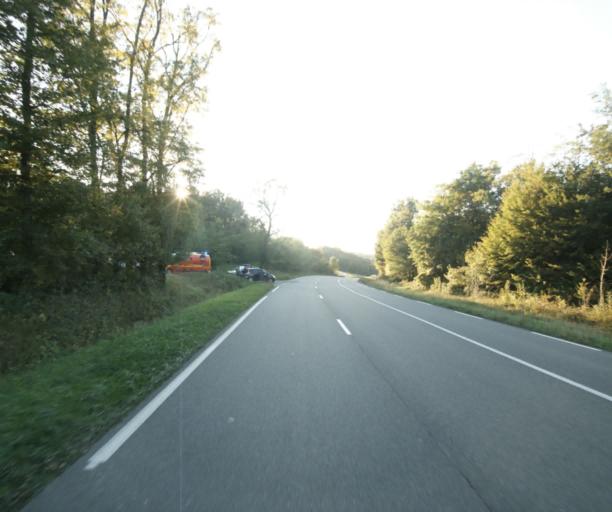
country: FR
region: Midi-Pyrenees
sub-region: Departement du Gers
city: Vic-Fezensac
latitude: 43.7600
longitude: 0.1867
